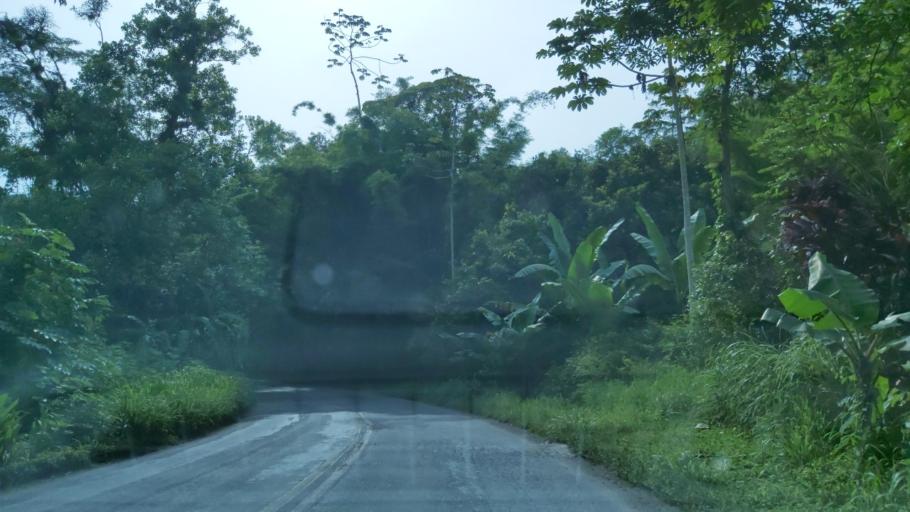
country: BR
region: Sao Paulo
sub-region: Miracatu
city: Miracatu
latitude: -24.0546
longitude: -47.5821
